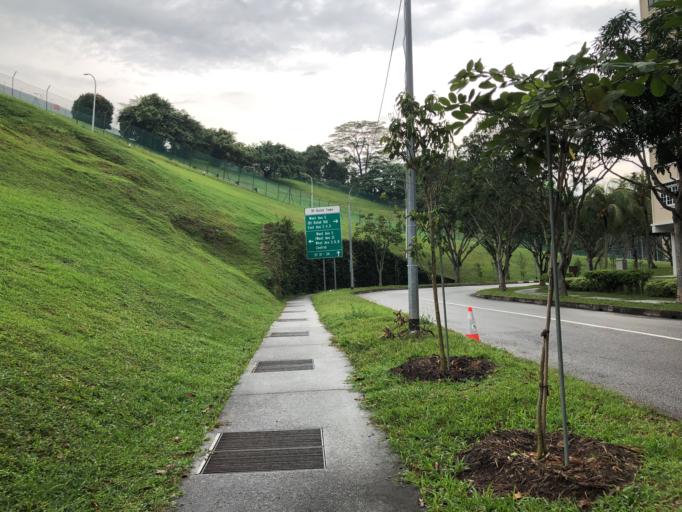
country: MY
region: Johor
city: Johor Bahru
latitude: 1.3556
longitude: 103.7499
